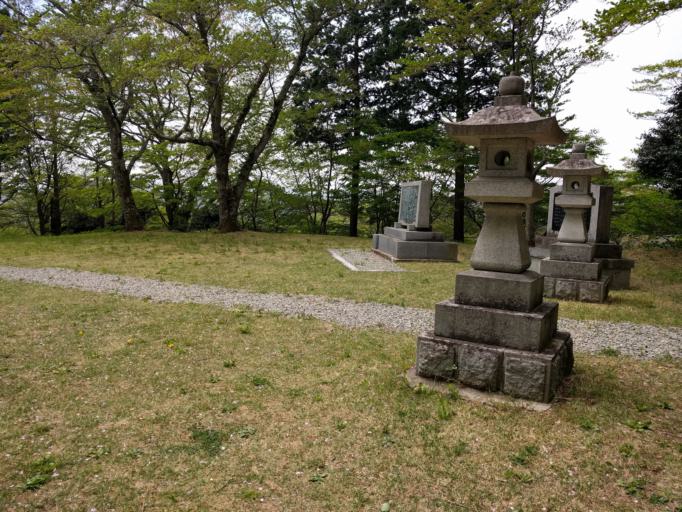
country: JP
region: Fukushima
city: Nihommatsu
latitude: 37.5987
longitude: 140.4276
